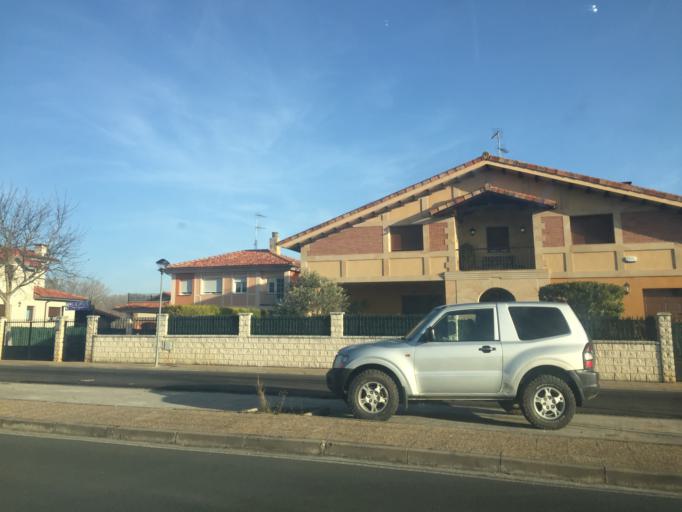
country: ES
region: Castille and Leon
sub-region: Provincia de Burgos
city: Medina de Pomar
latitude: 42.9390
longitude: -3.5848
